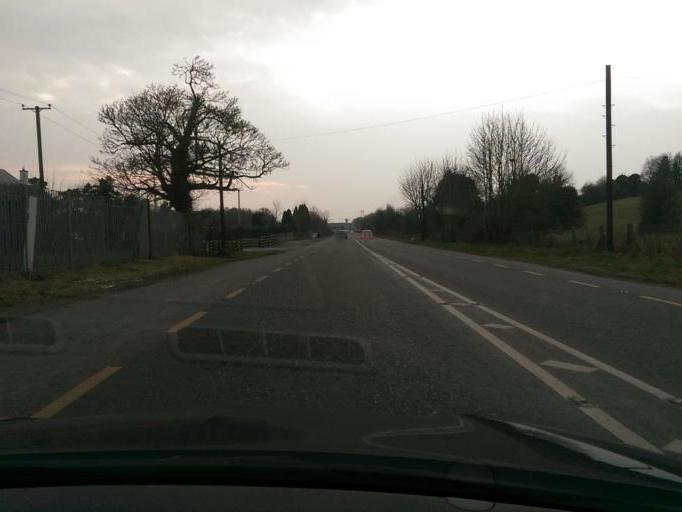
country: IE
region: Leinster
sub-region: An Iarmhi
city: Athlone
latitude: 53.4398
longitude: -7.8913
